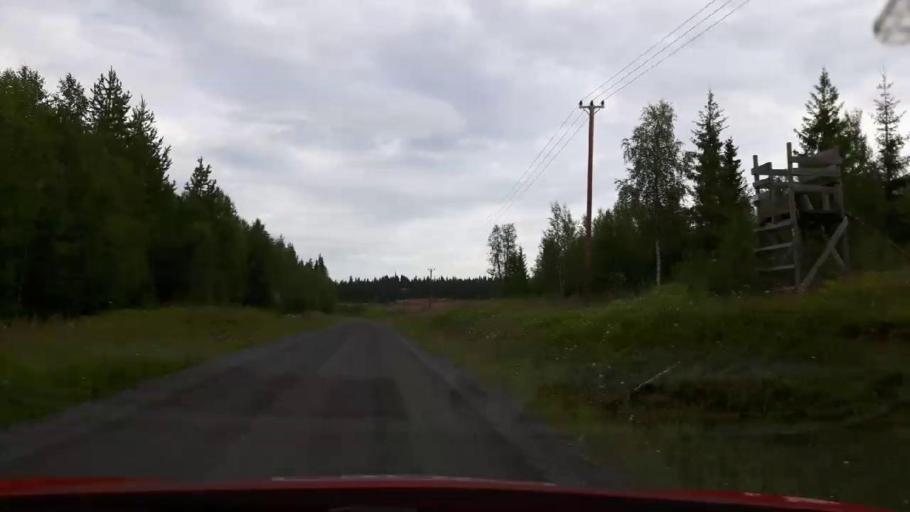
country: SE
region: Jaemtland
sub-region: Stroemsunds Kommun
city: Stroemsund
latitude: 63.4770
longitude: 15.2982
